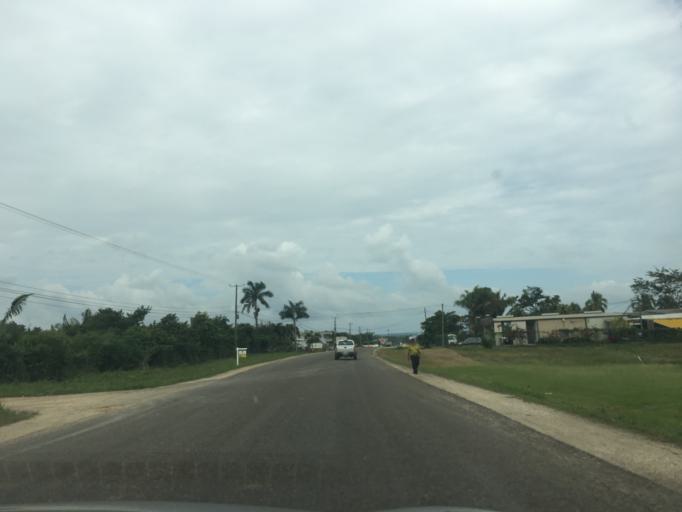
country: BZ
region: Cayo
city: Belmopan
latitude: 17.2422
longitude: -88.7826
